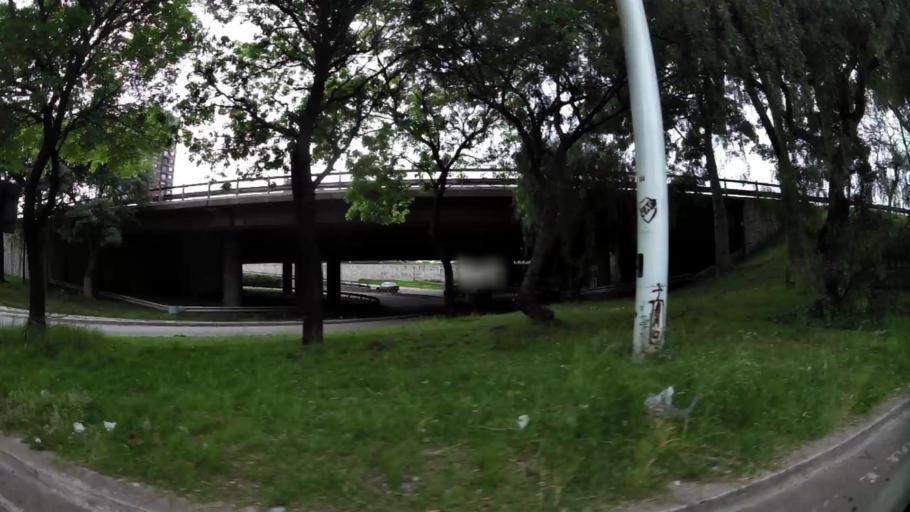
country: AR
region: Buenos Aires
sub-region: Partido de Vicente Lopez
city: Olivos
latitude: -34.5395
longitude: -58.4779
